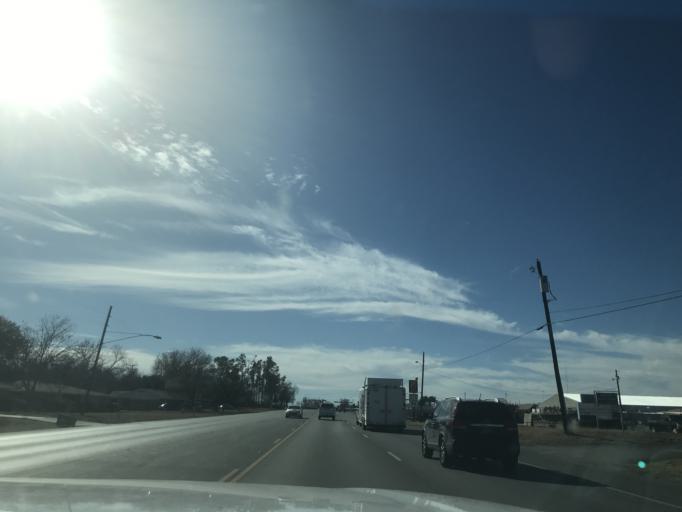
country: US
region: Texas
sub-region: Erath County
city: Stephenville
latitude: 32.2065
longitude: -98.2071
